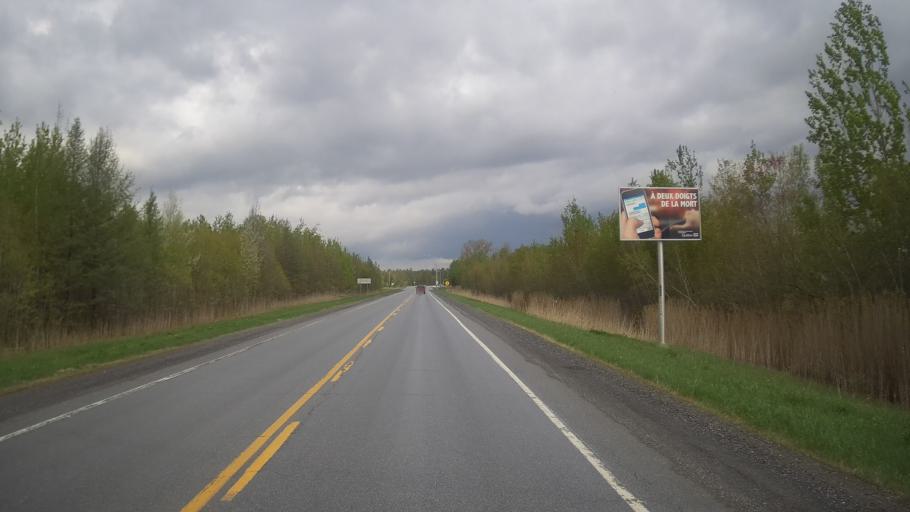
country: CA
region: Quebec
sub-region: Monteregie
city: Farnham
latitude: 45.2784
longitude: -72.9932
